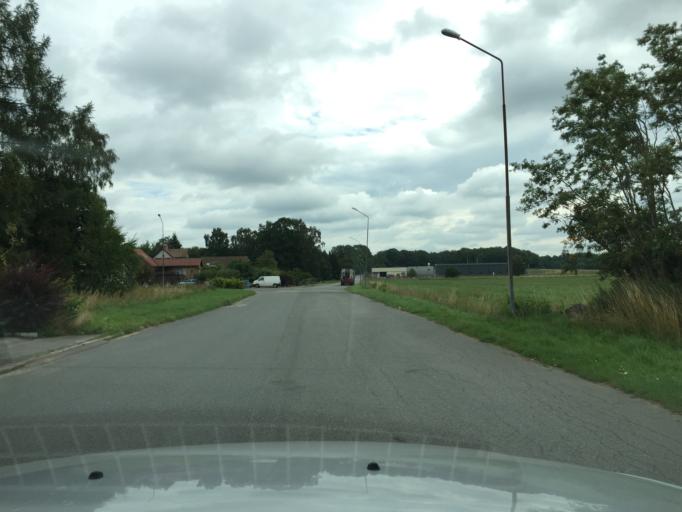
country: SE
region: Skane
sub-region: Hassleholms Kommun
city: Sosdala
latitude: 56.0355
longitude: 13.6830
